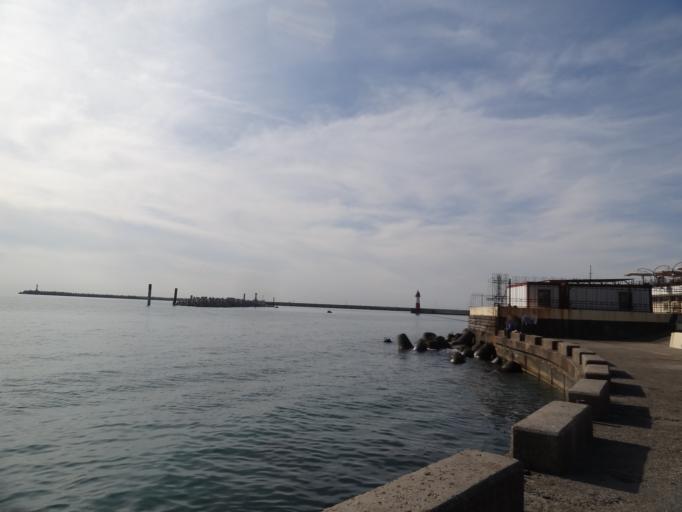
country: RU
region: Krasnodarskiy
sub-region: Sochi City
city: Sochi
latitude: 43.5789
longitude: 39.7185
